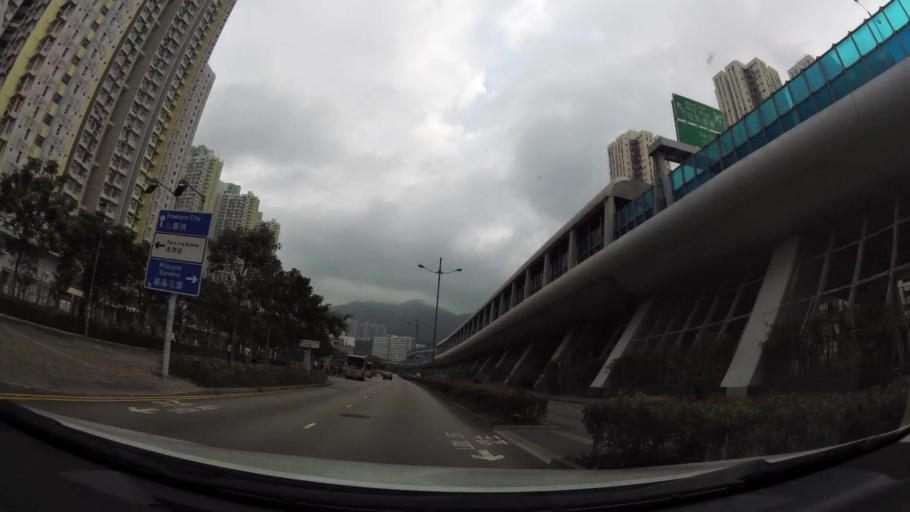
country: HK
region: Kowloon City
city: Kowloon
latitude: 22.3296
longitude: 114.2048
